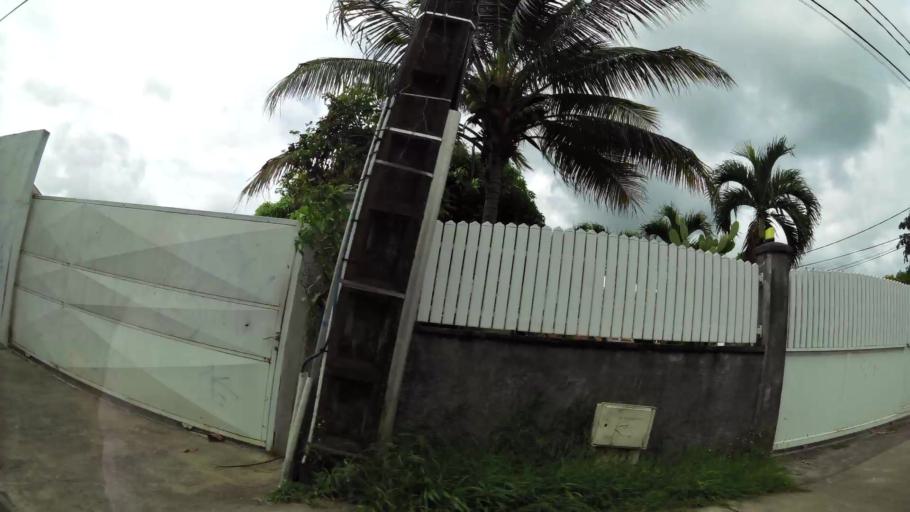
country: GP
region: Guadeloupe
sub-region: Guadeloupe
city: Baie-Mahault
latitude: 16.2545
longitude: -61.5801
